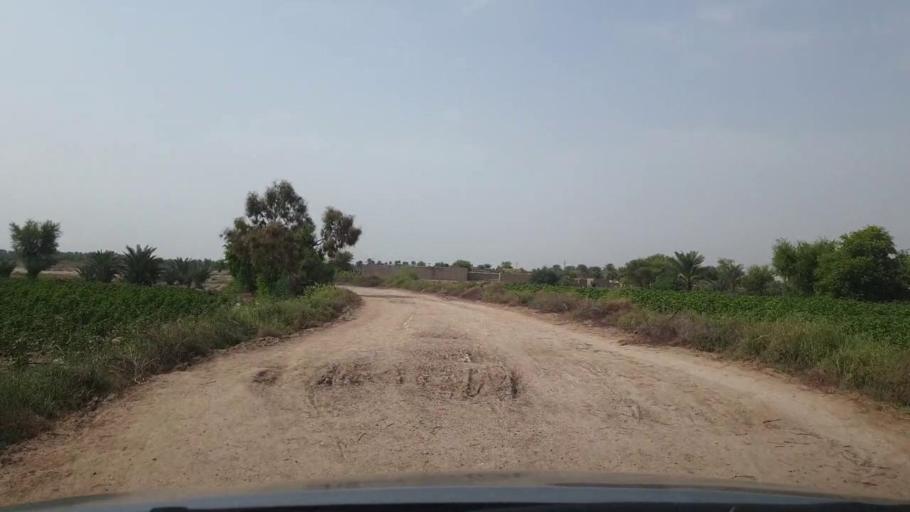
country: PK
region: Sindh
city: Rohri
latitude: 27.6639
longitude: 69.0130
